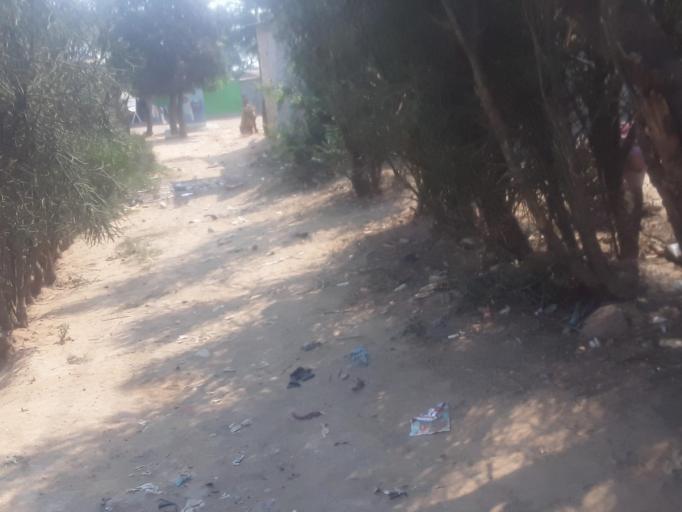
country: ZM
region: Lusaka
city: Lusaka
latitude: -15.3527
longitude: 28.2894
